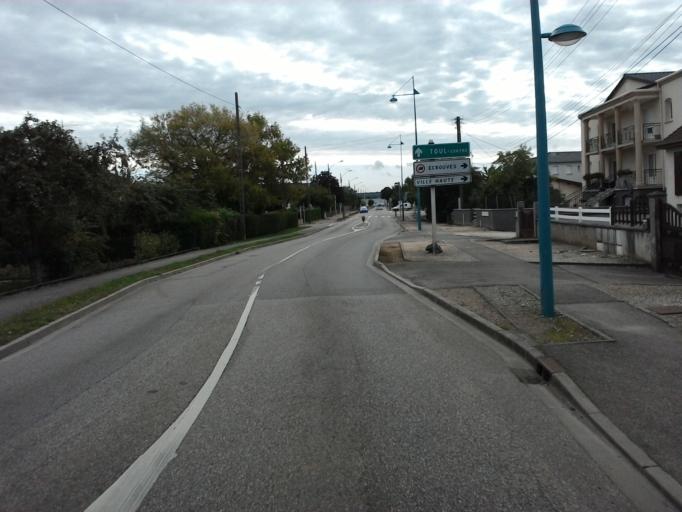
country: FR
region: Lorraine
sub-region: Departement de Meurthe-et-Moselle
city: Toul
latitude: 48.6938
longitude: 5.8980
